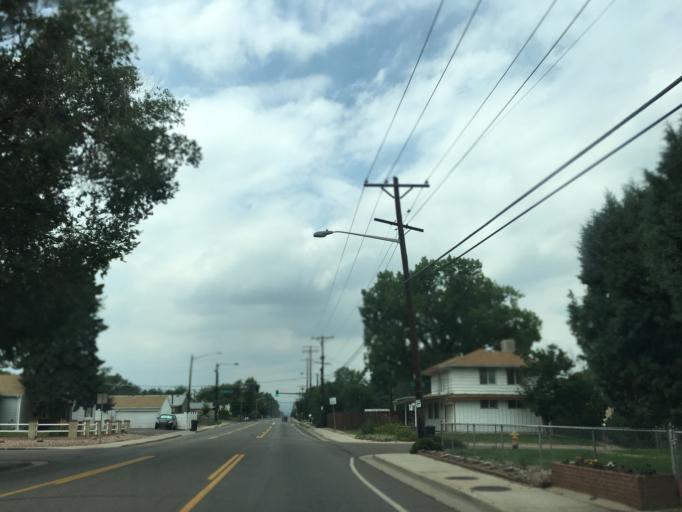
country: US
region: Colorado
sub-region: Arapahoe County
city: Sheridan
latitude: 39.6822
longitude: -105.0328
